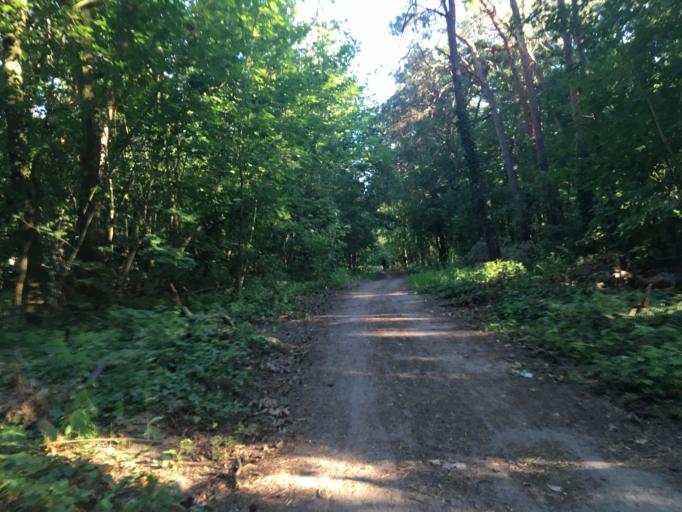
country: DE
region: Berlin
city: Grunau
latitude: 52.4169
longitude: 13.5725
